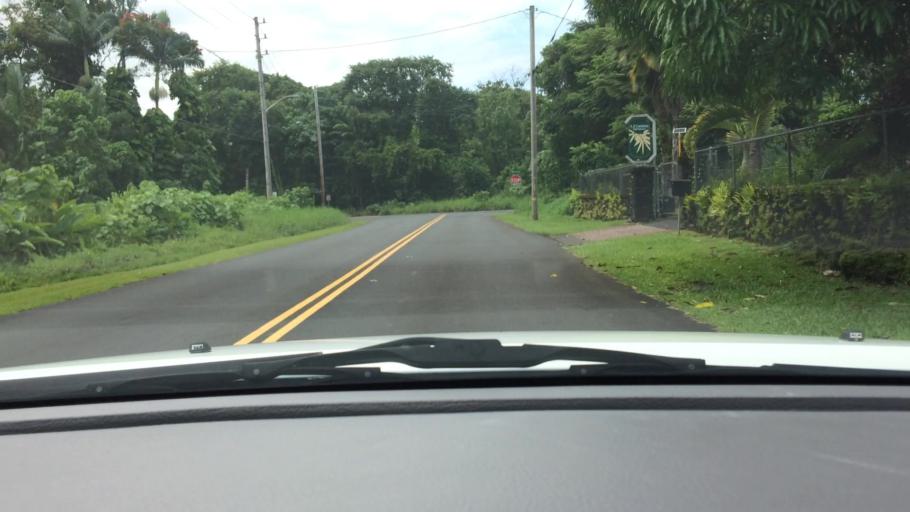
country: US
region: Hawaii
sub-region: Hawaii County
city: Hilo
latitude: 19.7157
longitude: -155.0714
